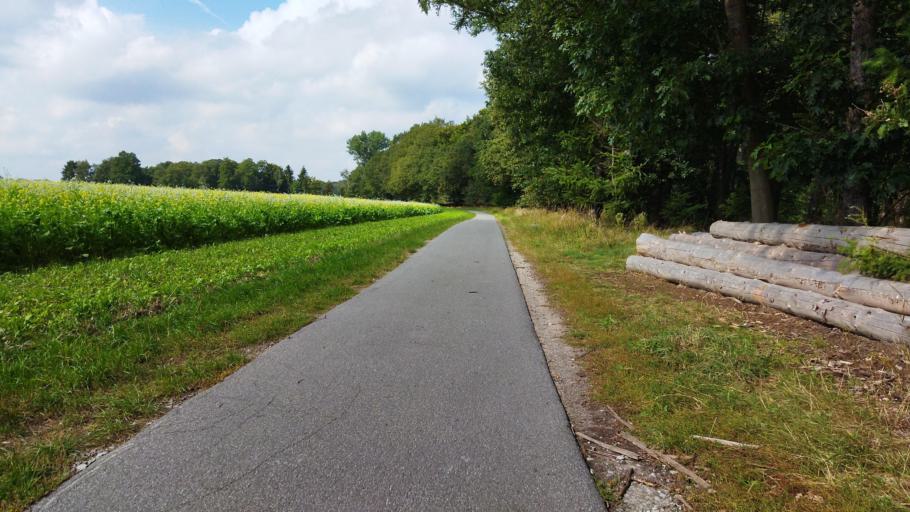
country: DE
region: North Rhine-Westphalia
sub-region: Regierungsbezirk Munster
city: Warendorf
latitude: 51.9622
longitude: 7.9265
